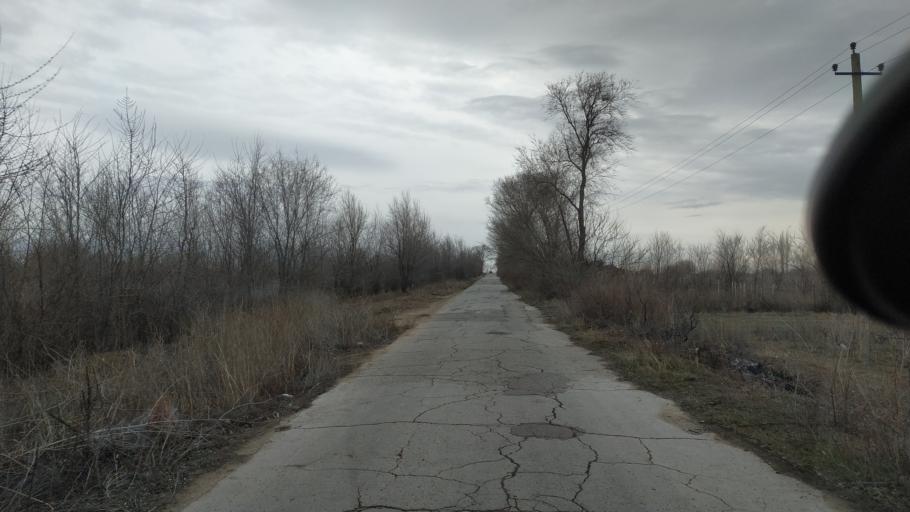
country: MD
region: Telenesti
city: Cocieri
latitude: 47.3268
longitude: 29.0942
